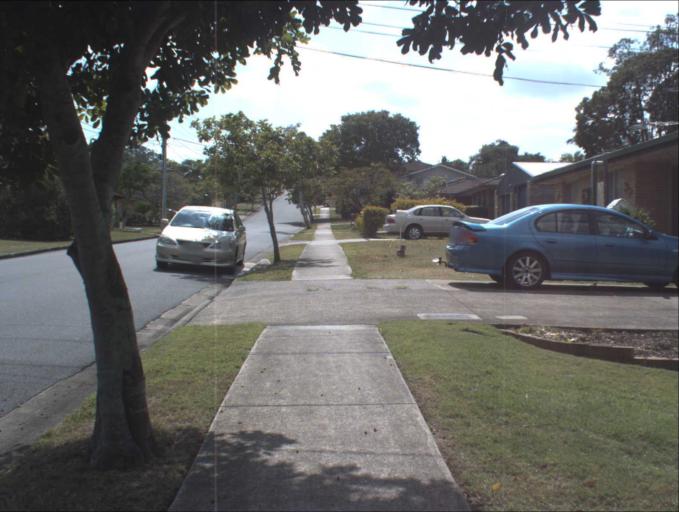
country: AU
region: Queensland
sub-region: Logan
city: Springwood
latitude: -27.6100
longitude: 153.1298
